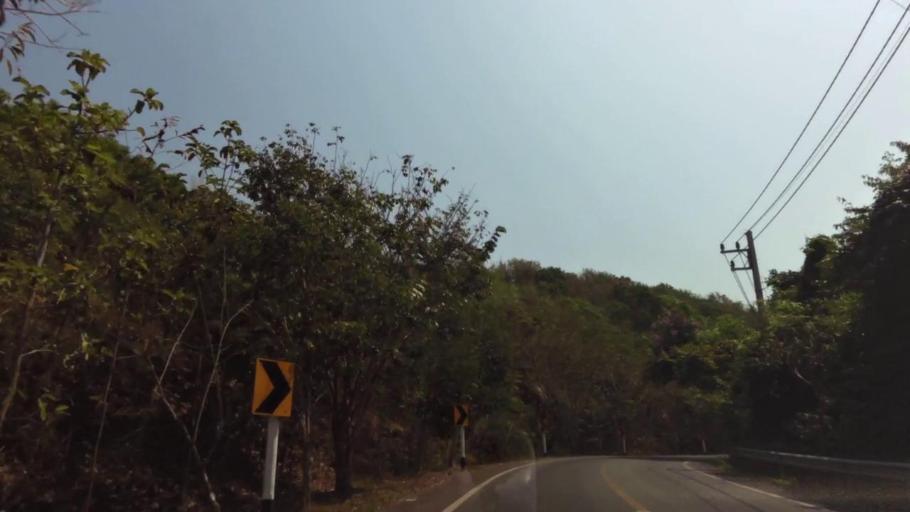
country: TH
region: Chanthaburi
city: Tha Mai
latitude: 12.5277
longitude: 101.9469
